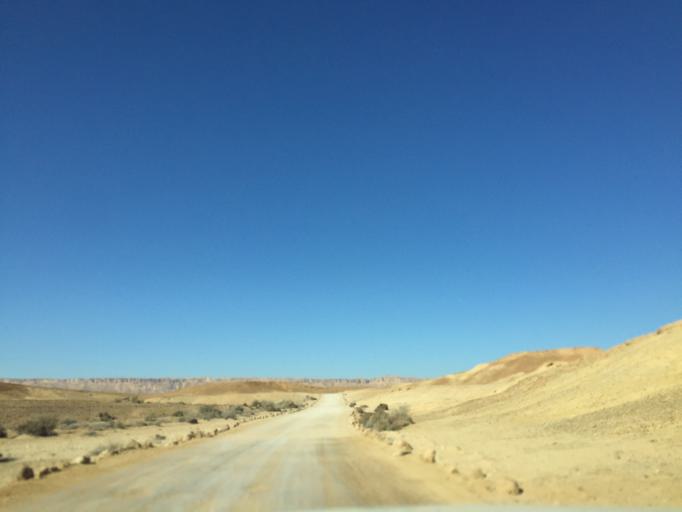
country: IL
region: Southern District
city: Mitzpe Ramon
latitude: 30.6159
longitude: 34.9314
